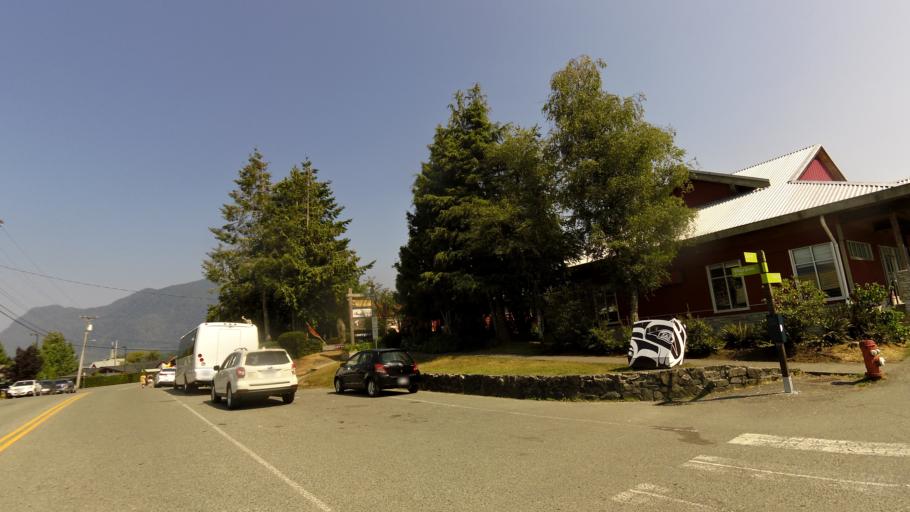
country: CA
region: British Columbia
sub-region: Regional District of Alberni-Clayoquot
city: Tofino
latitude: 49.1527
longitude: -125.9085
